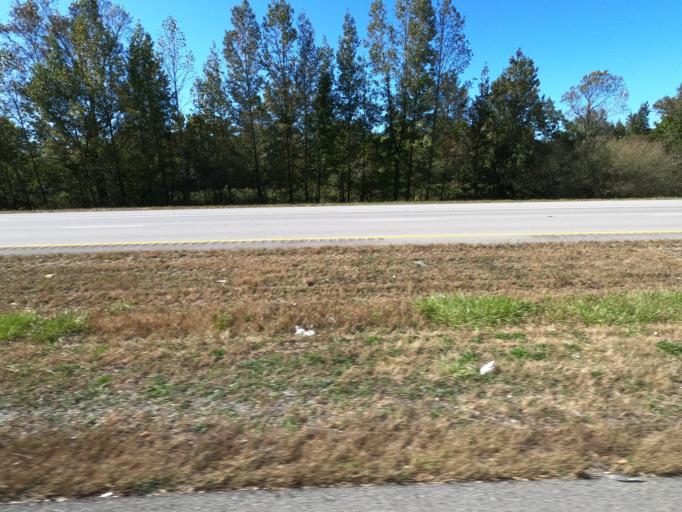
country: US
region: Tennessee
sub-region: Maury County
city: Mount Pleasant
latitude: 35.4192
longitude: -87.2821
